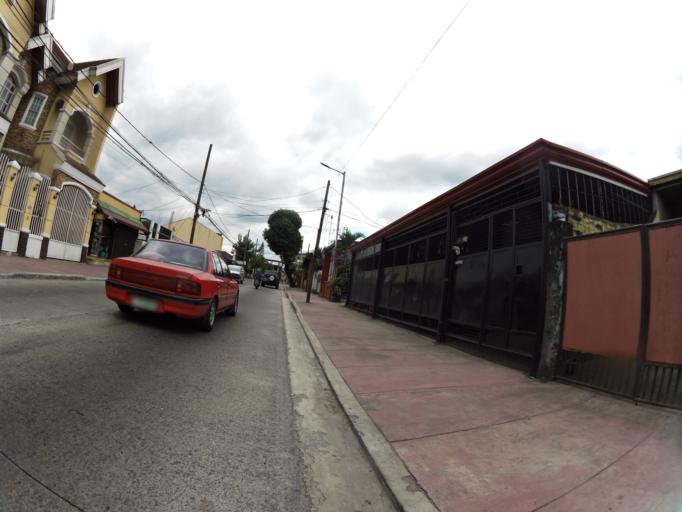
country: PH
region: Calabarzon
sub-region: Province of Rizal
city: Antipolo
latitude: 14.6371
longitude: 121.1196
